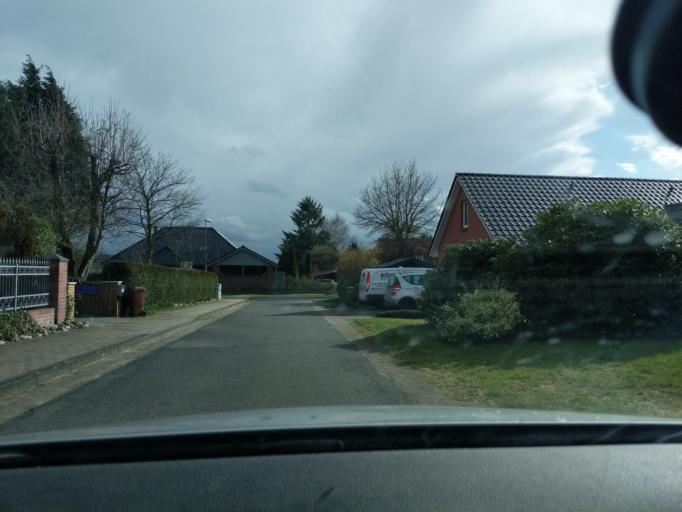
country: DE
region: Lower Saxony
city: Oldendorf
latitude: 53.5862
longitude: 9.2433
